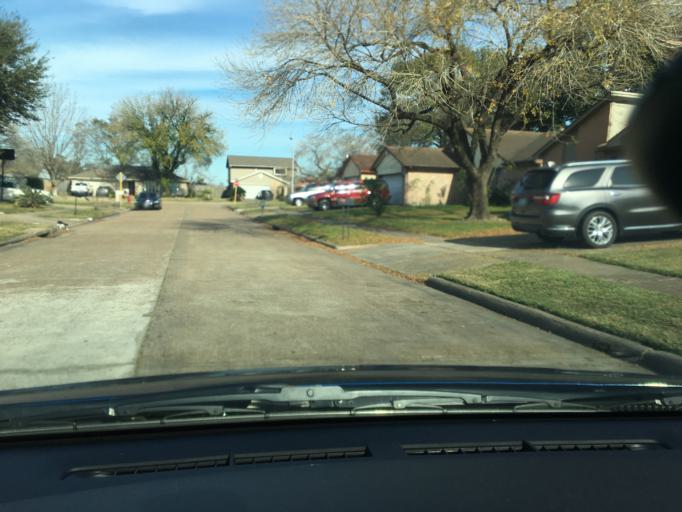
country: US
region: Texas
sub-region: Harris County
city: Cloverleaf
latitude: 29.8078
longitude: -95.1593
